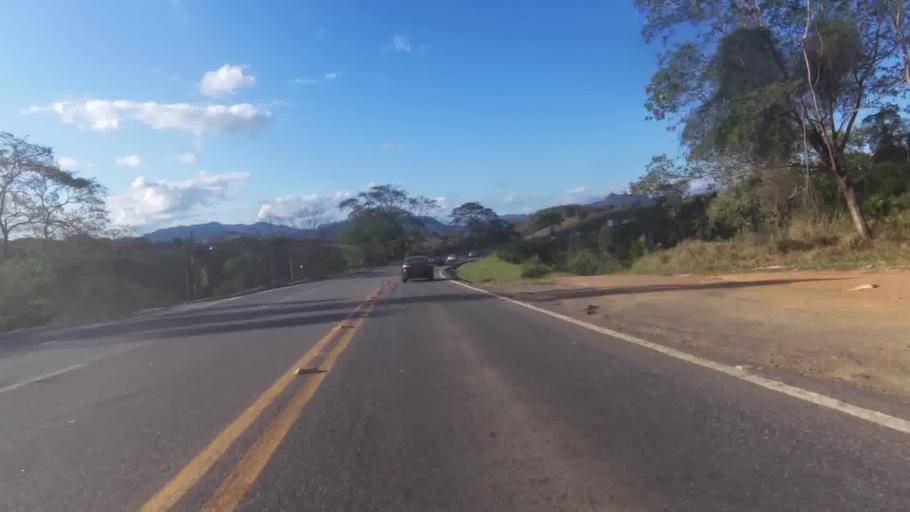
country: BR
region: Espirito Santo
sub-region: Alfredo Chaves
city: Alfredo Chaves
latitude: -20.7007
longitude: -40.7158
